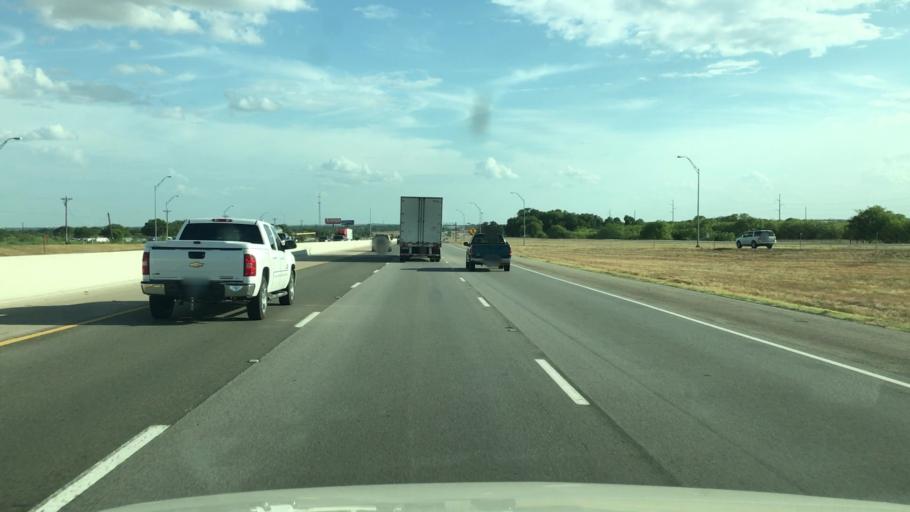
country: US
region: Texas
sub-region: Williamson County
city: Serenada
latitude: 30.7170
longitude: -97.6466
